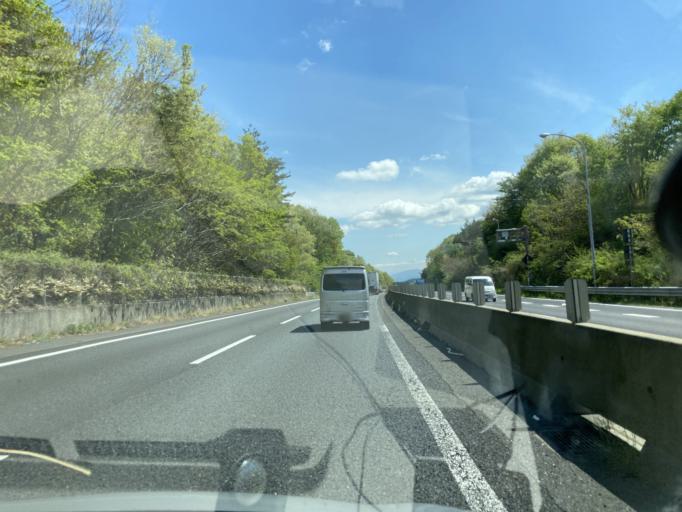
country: JP
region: Mie
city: Nabari
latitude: 34.6446
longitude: 136.0101
